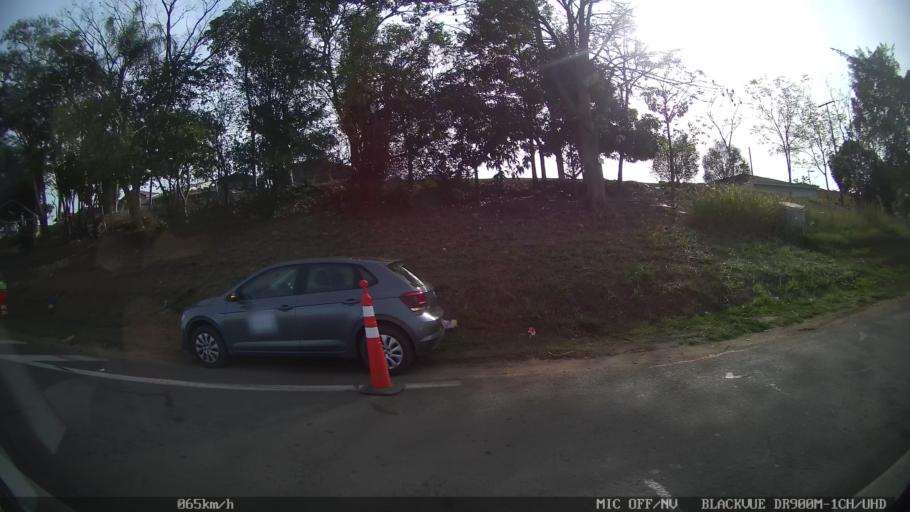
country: BR
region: Sao Paulo
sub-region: Piracicaba
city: Piracicaba
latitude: -22.6835
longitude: -47.6847
